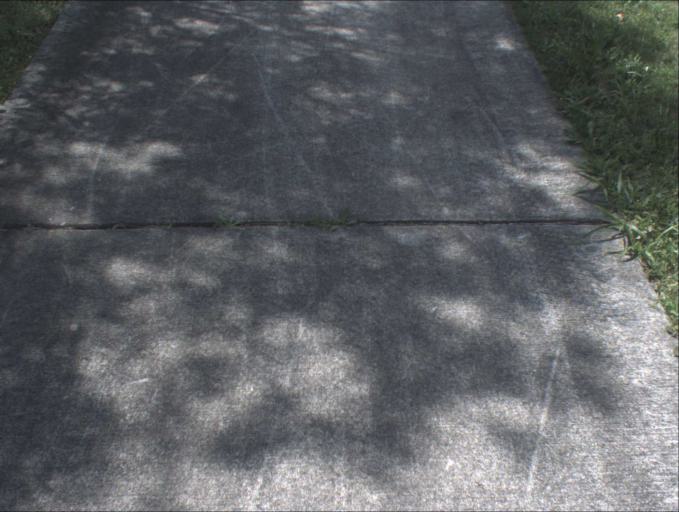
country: AU
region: Queensland
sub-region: Logan
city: Woodridge
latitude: -27.6683
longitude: 153.0841
